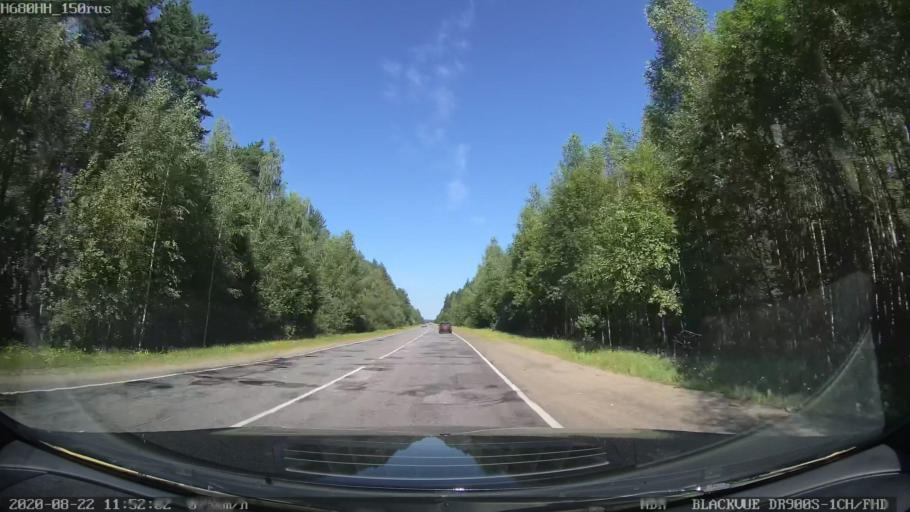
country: RU
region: Tverskaya
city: Sakharovo
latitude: 57.1103
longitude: 36.1195
